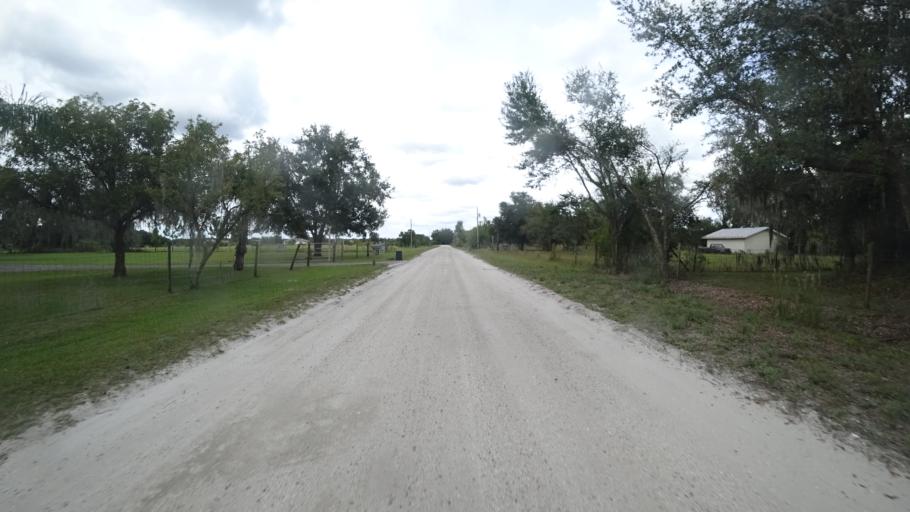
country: US
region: Florida
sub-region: Sarasota County
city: Lake Sarasota
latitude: 27.3993
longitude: -82.2664
